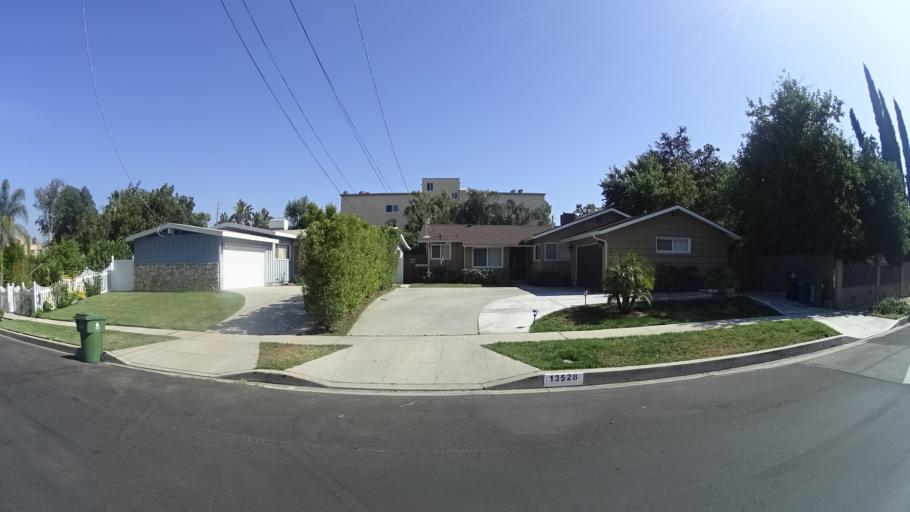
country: US
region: California
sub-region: Los Angeles County
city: Van Nuys
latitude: 34.1949
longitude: -118.4278
